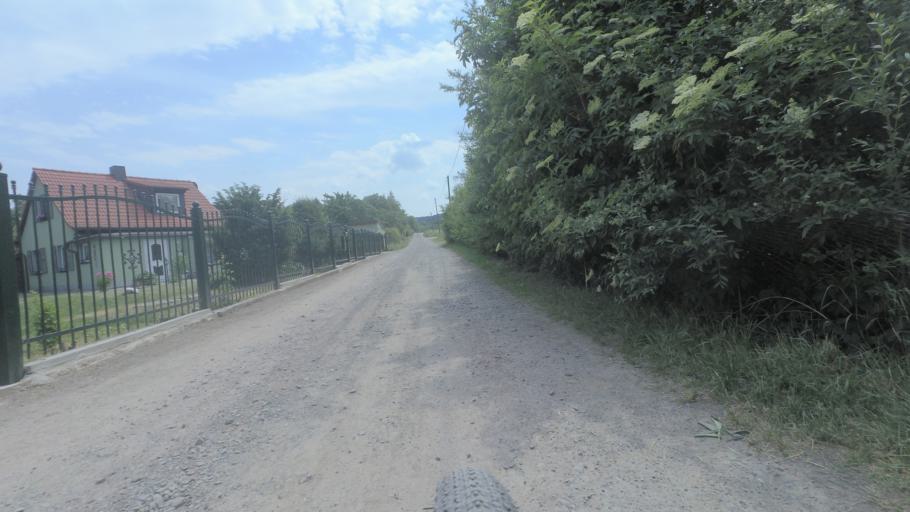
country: DE
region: Saxony-Anhalt
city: Rieder
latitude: 51.7306
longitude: 11.1552
